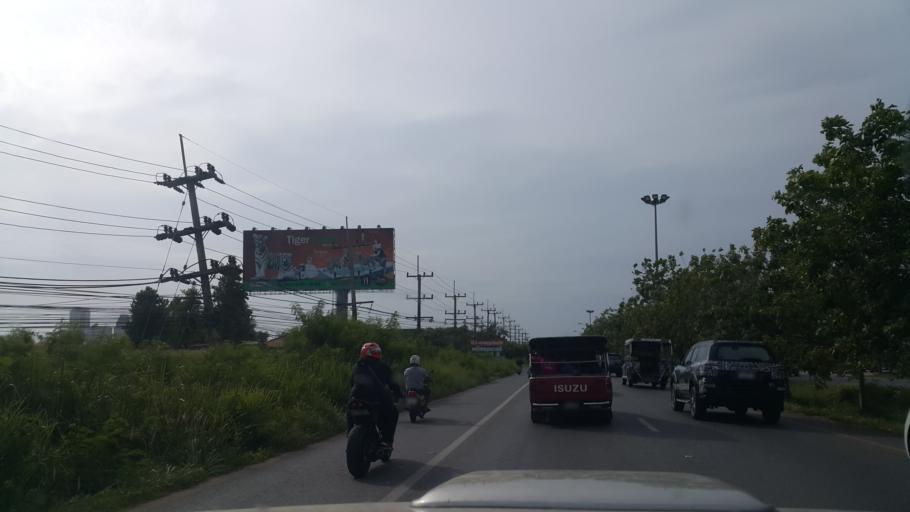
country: TH
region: Chon Buri
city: Phatthaya
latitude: 12.8600
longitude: 100.9077
